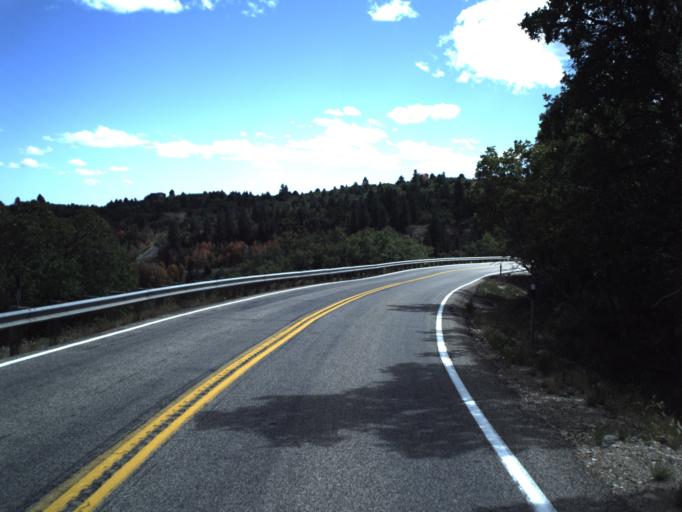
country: US
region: Utah
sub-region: Garfield County
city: Panguitch
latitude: 37.4946
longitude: -112.5303
